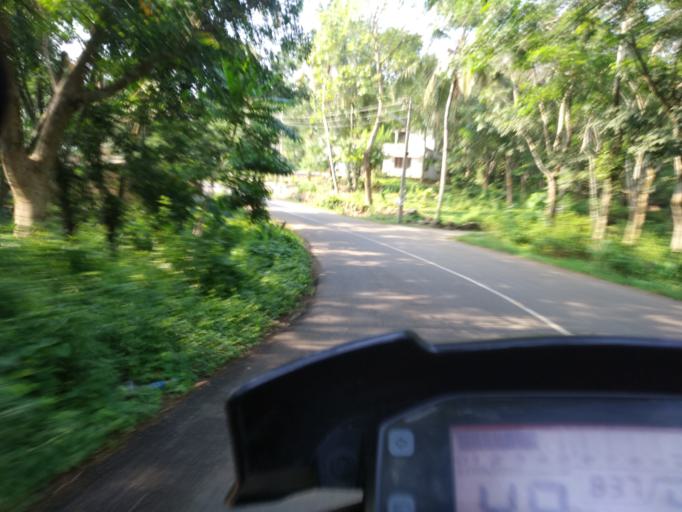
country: IN
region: Kerala
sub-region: Ernakulam
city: Ramamangalam
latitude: 9.9119
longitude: 76.4370
